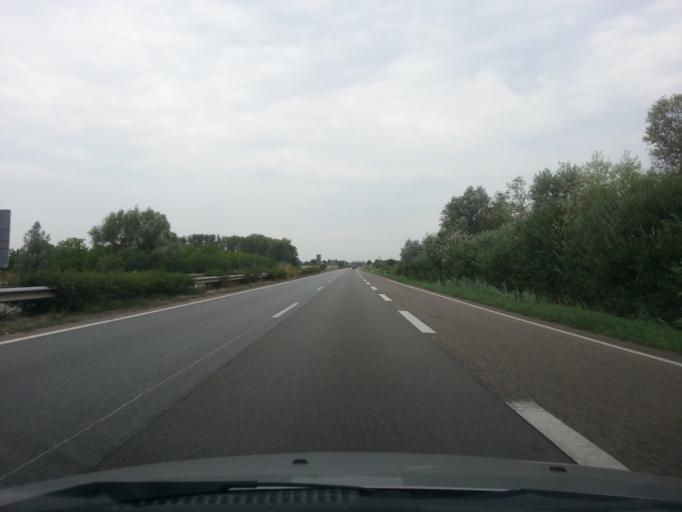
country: DE
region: Rheinland-Pfalz
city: Kirrweiler
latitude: 49.2843
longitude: 8.1529
